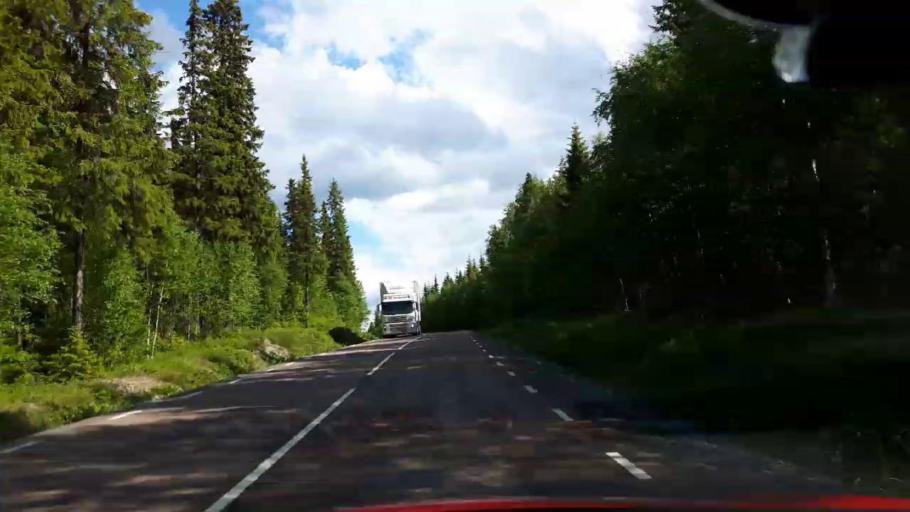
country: SE
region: Jaemtland
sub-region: Krokoms Kommun
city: Valla
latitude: 63.9652
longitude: 14.1729
